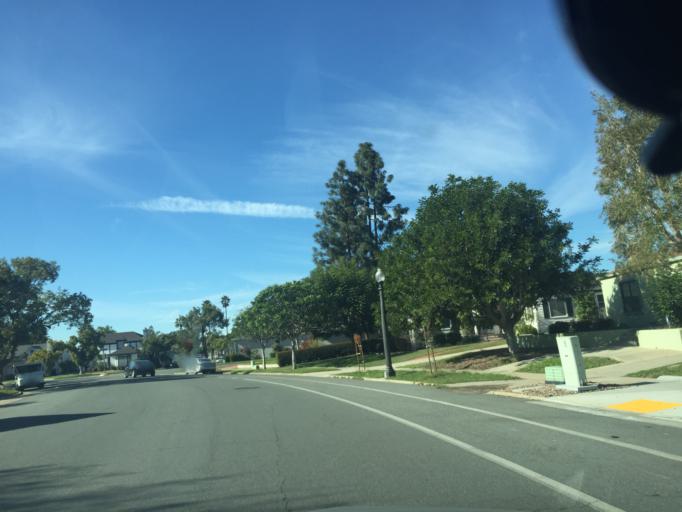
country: US
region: California
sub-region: San Diego County
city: Lemon Grove
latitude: 32.7622
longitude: -117.0905
